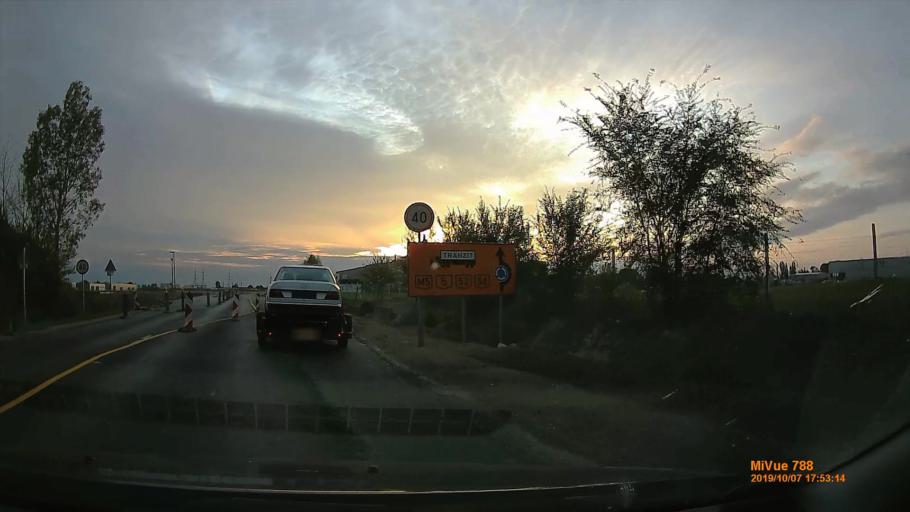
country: HU
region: Bacs-Kiskun
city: Kecskemet
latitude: 46.8797
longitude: 19.7143
